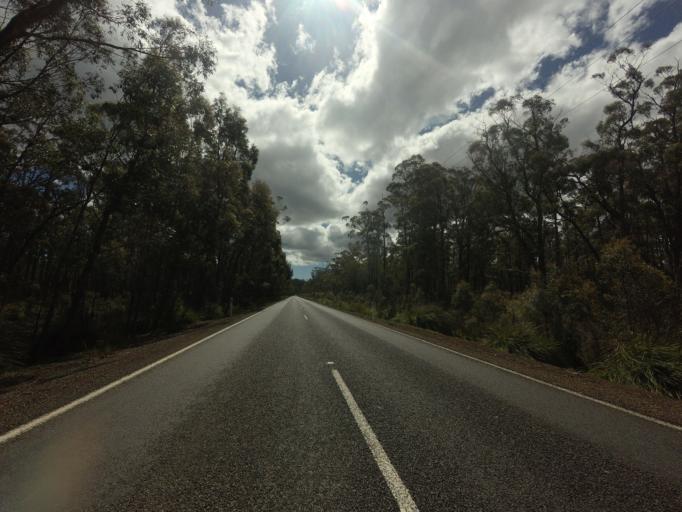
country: AU
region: Tasmania
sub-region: Northern Midlands
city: Evandale
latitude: -42.0208
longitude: 147.7443
